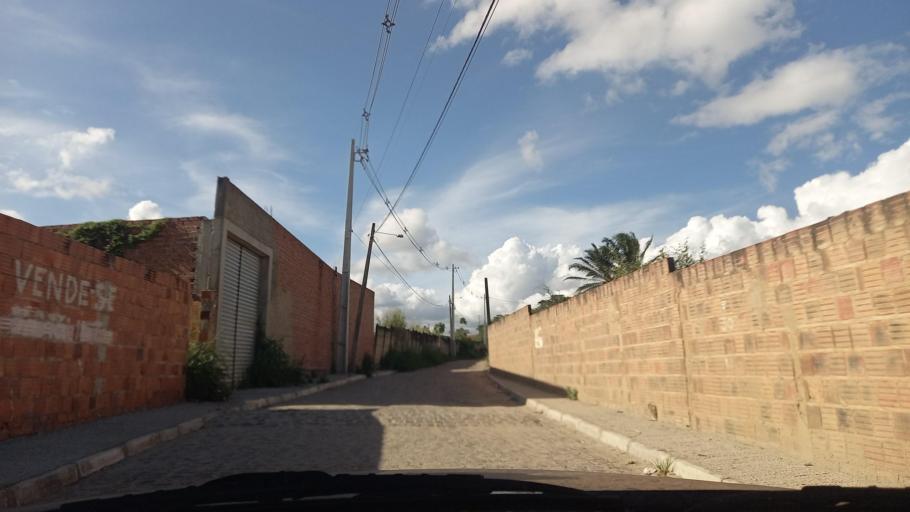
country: BR
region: Pernambuco
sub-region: Gravata
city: Gravata
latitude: -8.1979
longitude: -35.5663
